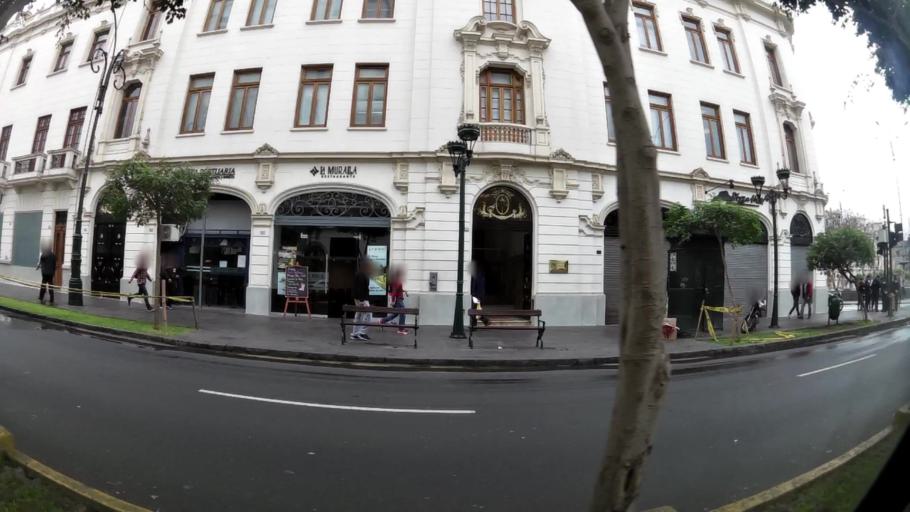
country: PE
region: Lima
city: Lima
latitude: -12.0521
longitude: -77.0339
